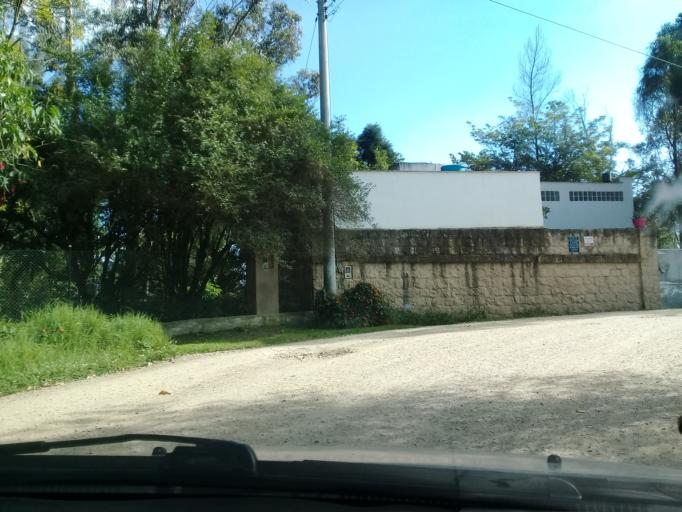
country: CO
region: Cundinamarca
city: Tabio
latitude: 4.9608
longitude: -74.0796
